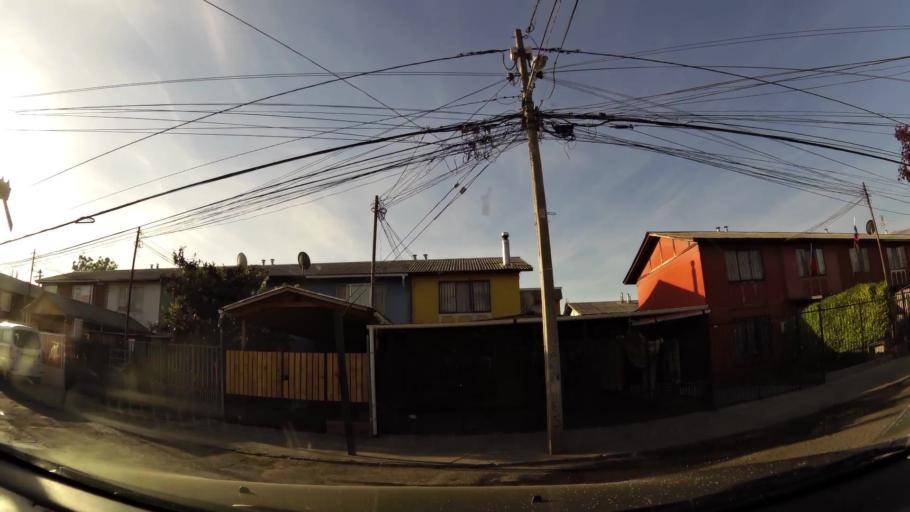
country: CL
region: Santiago Metropolitan
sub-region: Provincia de Cordillera
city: Puente Alto
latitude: -33.5976
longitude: -70.5602
